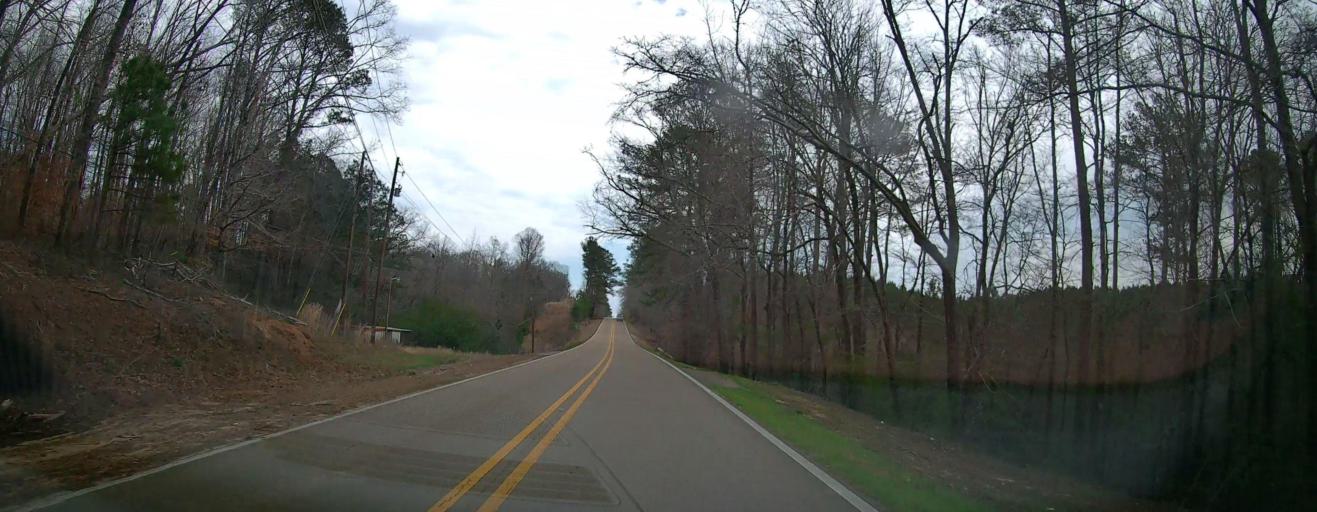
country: US
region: Mississippi
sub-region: Itawamba County
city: Fulton
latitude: 34.2488
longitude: -88.2984
